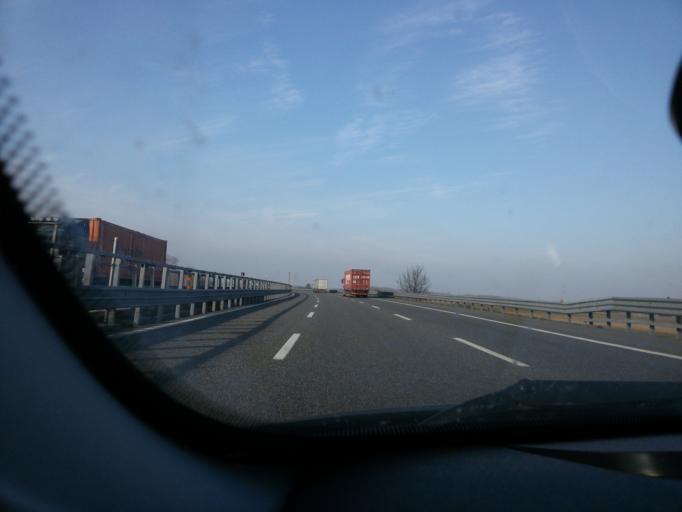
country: IT
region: Piedmont
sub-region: Provincia di Alessandria
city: Mirabello Monferrato
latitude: 45.0246
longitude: 8.5379
